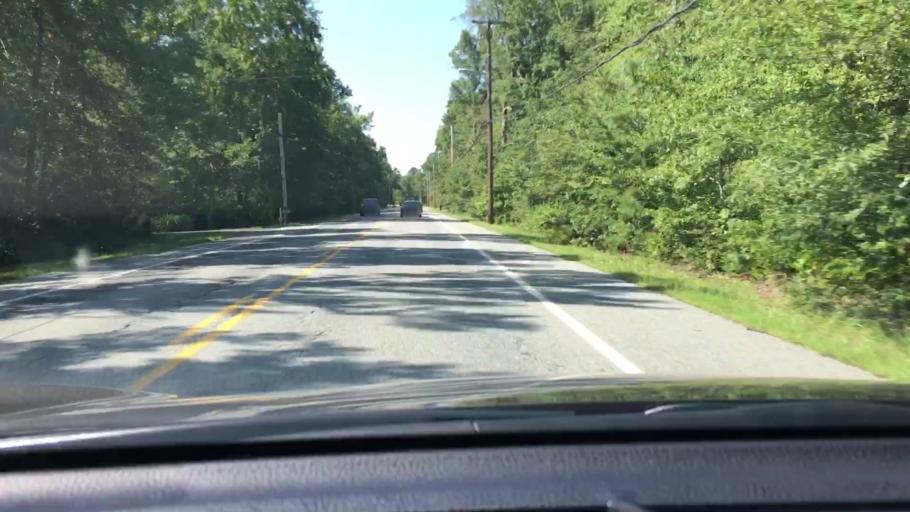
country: US
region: New Jersey
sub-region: Cape May County
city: Woodbine
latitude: 39.2888
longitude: -74.7881
